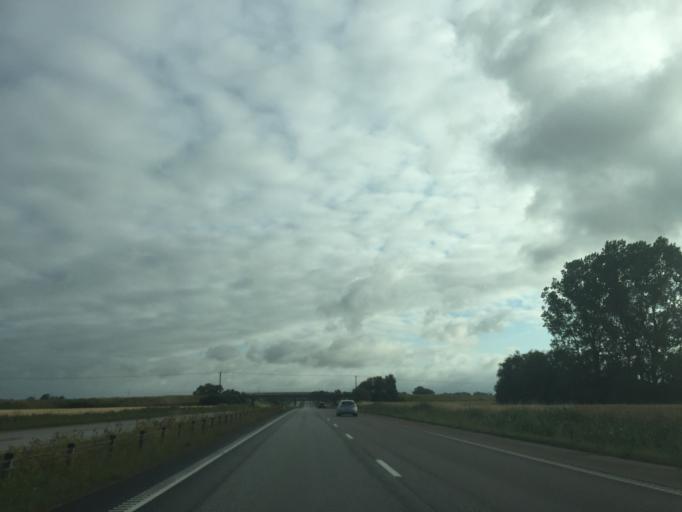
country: SE
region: Skane
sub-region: Angelholms Kommun
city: Strovelstorp
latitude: 56.1303
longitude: 12.8308
